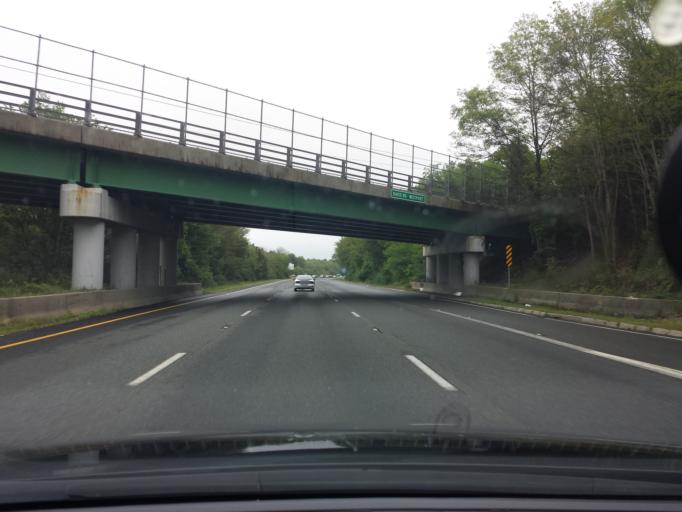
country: US
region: Massachusetts
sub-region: Bristol County
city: North Westport
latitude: 41.6725
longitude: -71.0883
